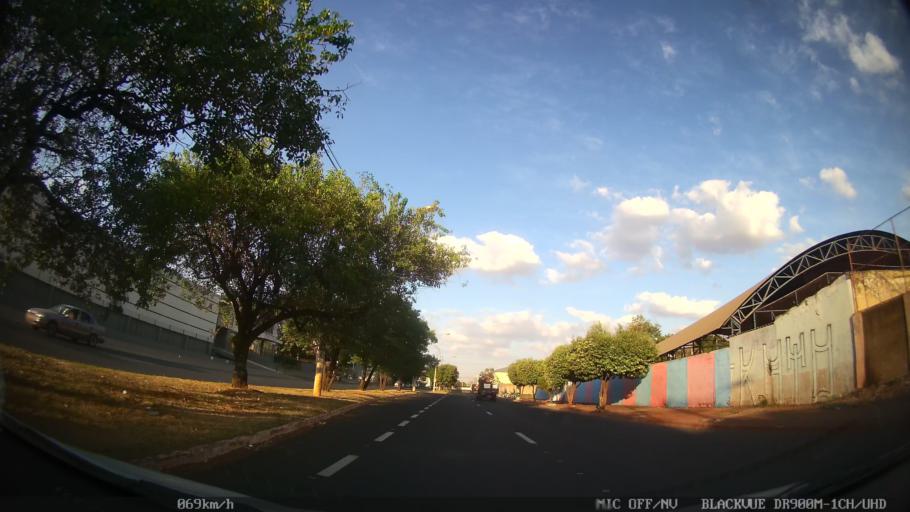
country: BR
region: Sao Paulo
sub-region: Ribeirao Preto
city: Ribeirao Preto
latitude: -21.1391
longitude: -47.7915
